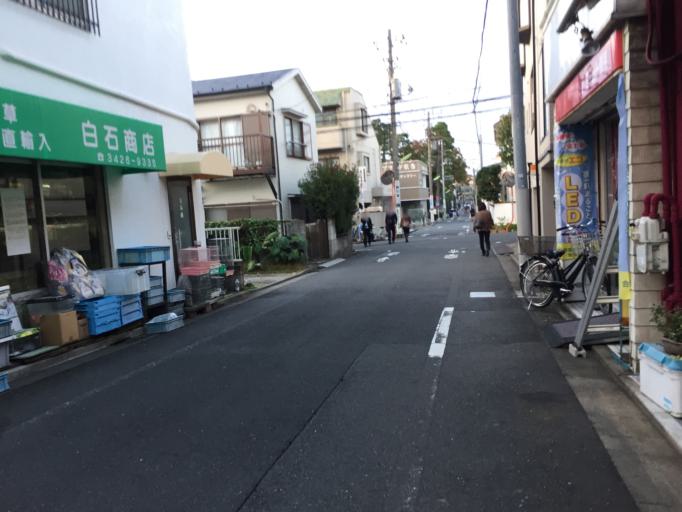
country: JP
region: Tokyo
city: Tokyo
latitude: 35.6321
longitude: 139.6452
